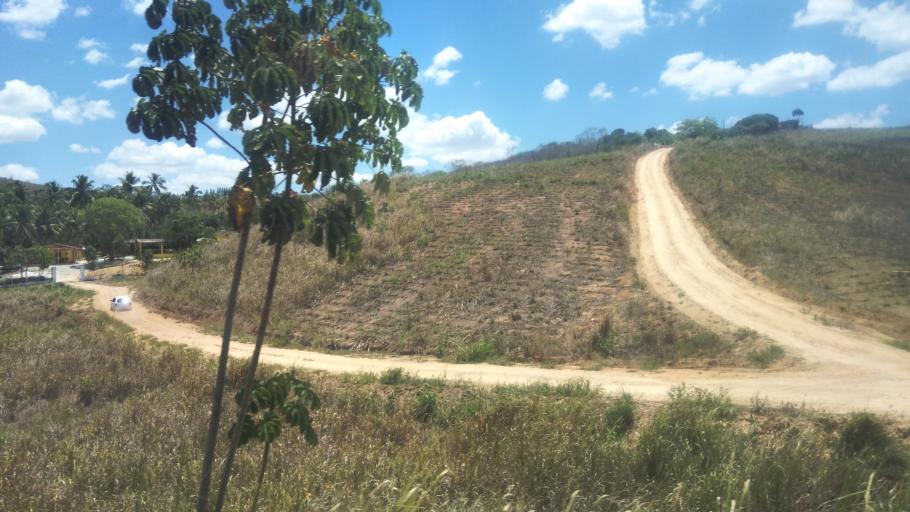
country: BR
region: Pernambuco
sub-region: Nazare Da Mata
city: Nazare da Mata
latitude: -7.7370
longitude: -35.3042
